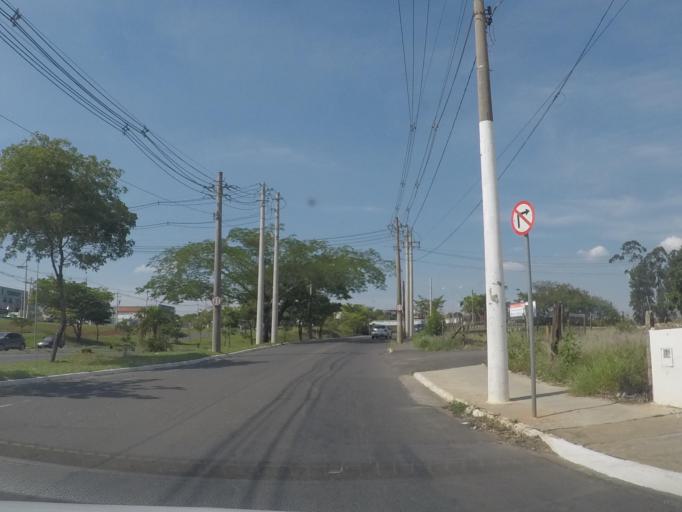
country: BR
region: Sao Paulo
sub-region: Sumare
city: Sumare
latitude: -22.8126
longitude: -47.2581
